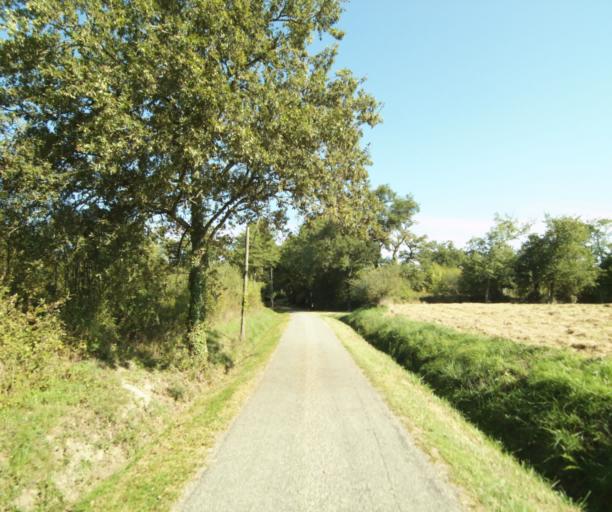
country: FR
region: Midi-Pyrenees
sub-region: Departement du Gers
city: Cazaubon
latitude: 43.9521
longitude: -0.0232
